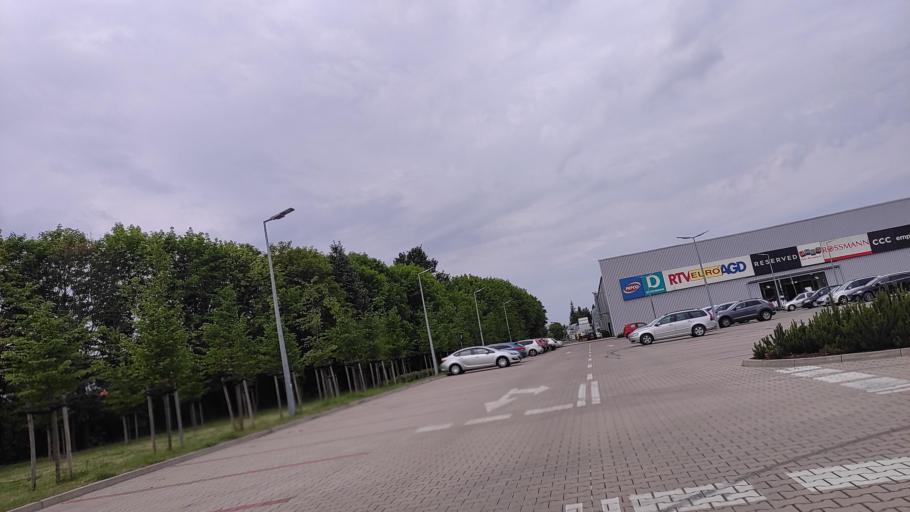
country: PL
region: Greater Poland Voivodeship
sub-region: Powiat poznanski
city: Swarzedz
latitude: 52.4036
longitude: 17.0978
